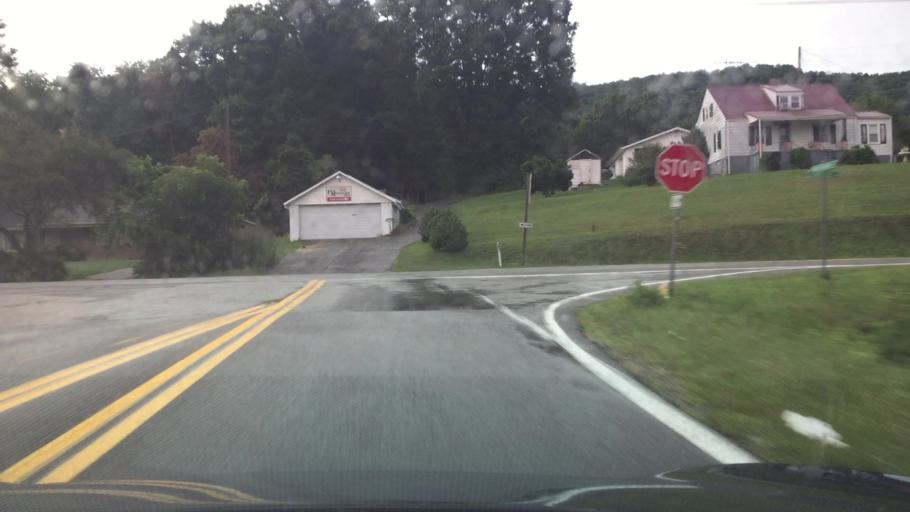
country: US
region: Virginia
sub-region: Pulaski County
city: Pulaski
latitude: 36.9527
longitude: -80.8823
